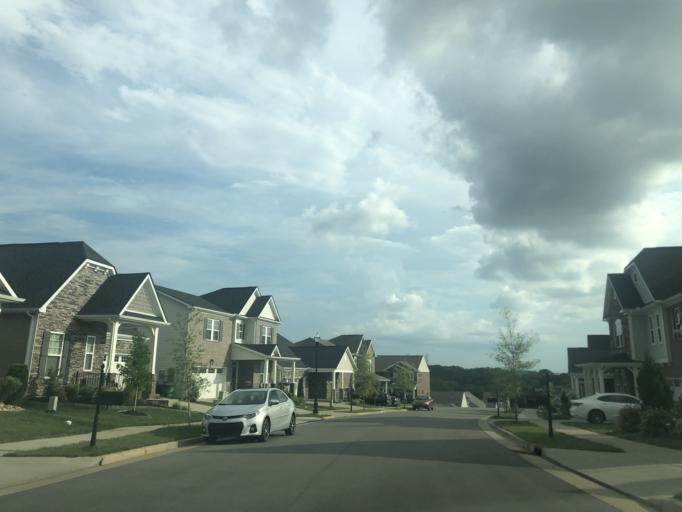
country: US
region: Tennessee
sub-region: Davidson County
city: Lakewood
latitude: 36.1667
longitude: -86.6233
